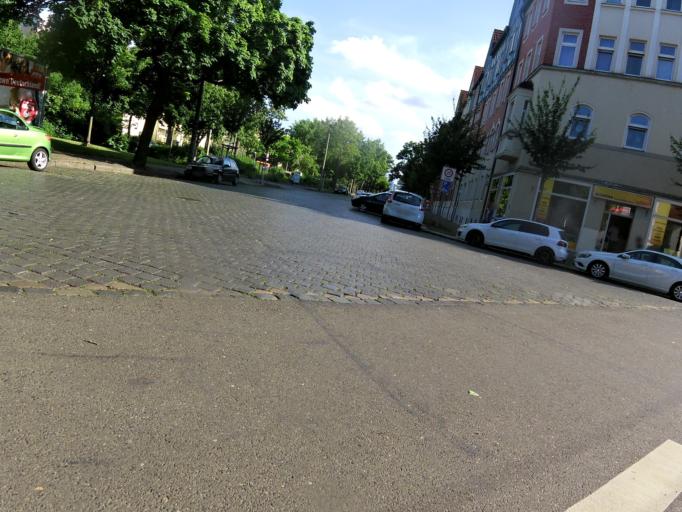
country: DE
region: Saxony
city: Leipzig
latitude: 51.3557
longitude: 12.4146
